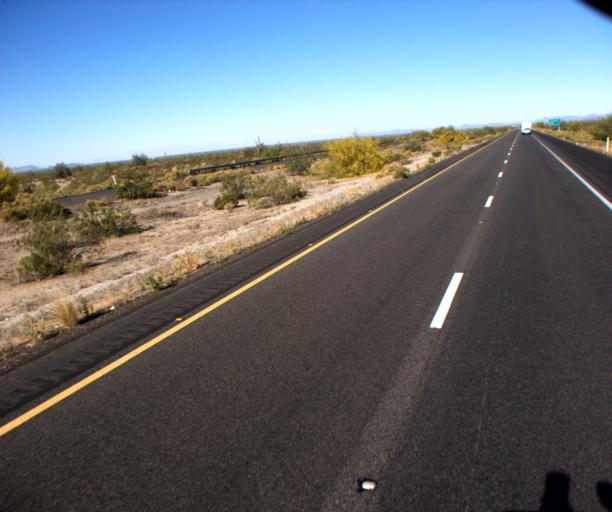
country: US
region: Arizona
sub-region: Maricopa County
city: Gila Bend
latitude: 32.9157
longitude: -112.6266
